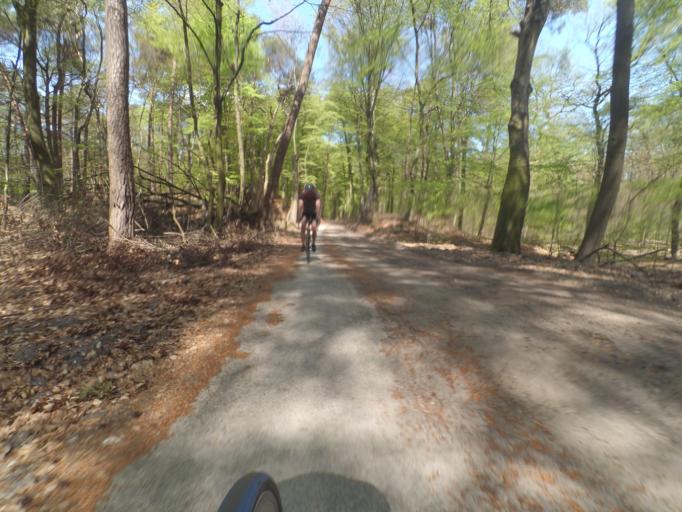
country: NL
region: Gelderland
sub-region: Gemeente Ermelo
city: Ermelo
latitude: 52.3210
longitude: 5.7035
